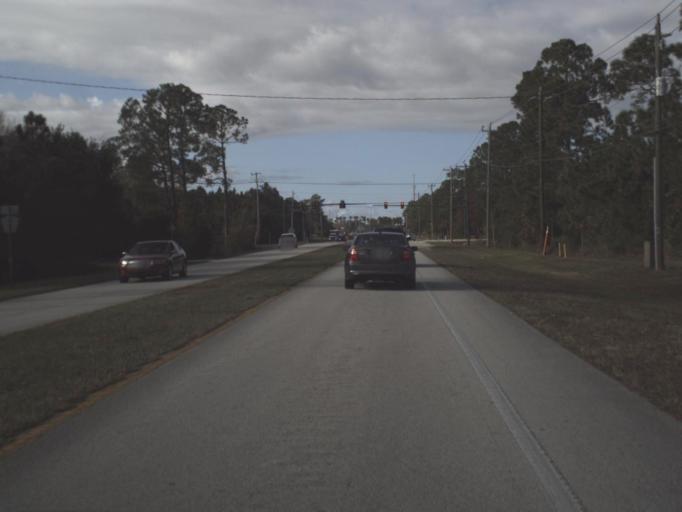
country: US
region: Florida
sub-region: Volusia County
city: Ormond Beach
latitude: 29.2487
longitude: -81.1078
